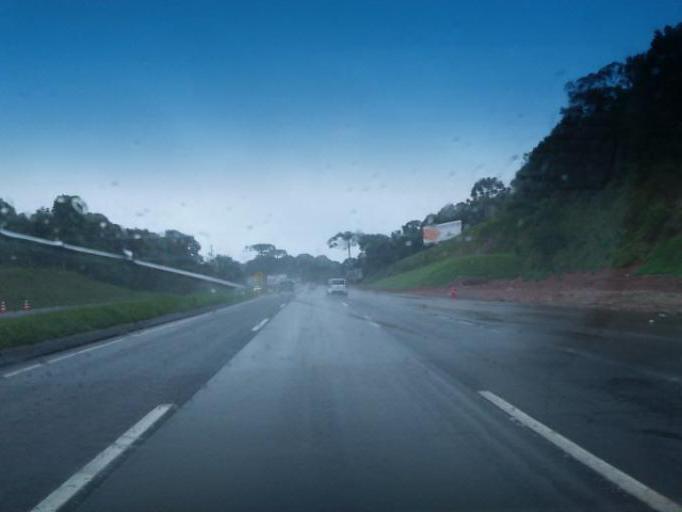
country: BR
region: Parana
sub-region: Sao Jose Dos Pinhais
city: Sao Jose dos Pinhais
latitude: -25.5924
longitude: -49.1721
